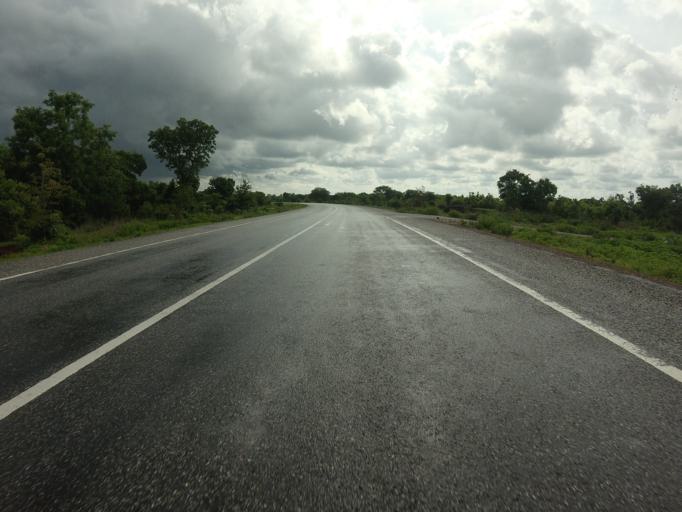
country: GH
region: Northern
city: Tamale
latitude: 9.1673
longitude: -1.4757
